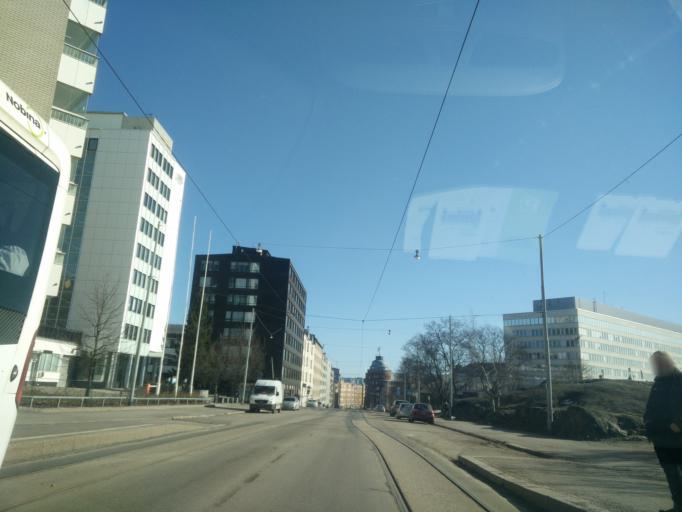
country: FI
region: Uusimaa
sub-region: Helsinki
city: Helsinki
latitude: 60.1828
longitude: 24.9454
